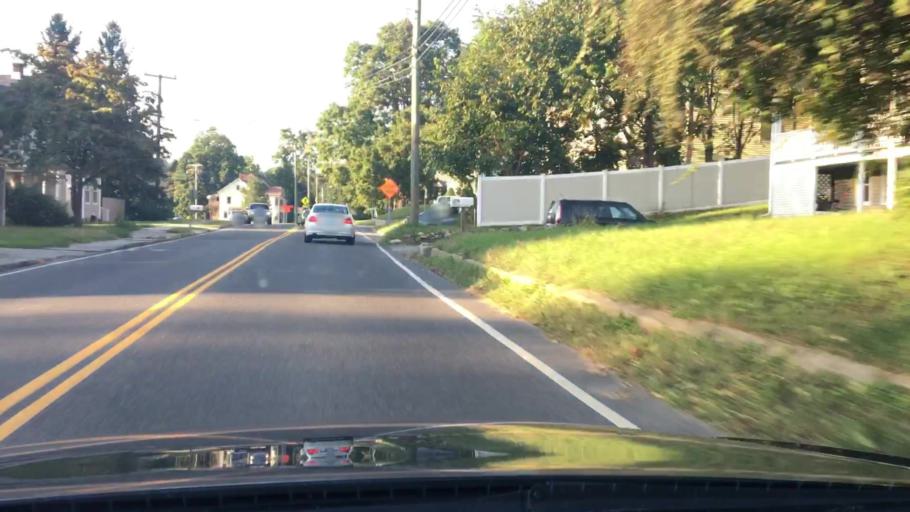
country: US
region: Connecticut
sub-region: Litchfield County
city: New Milford
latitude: 41.5723
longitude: -73.4072
